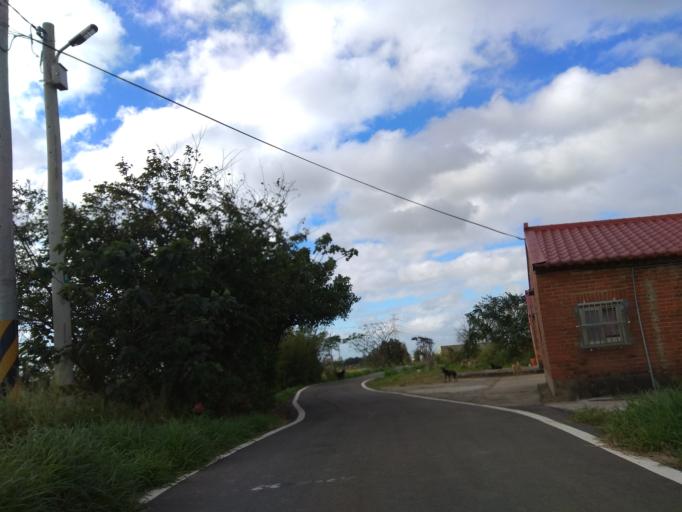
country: TW
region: Taiwan
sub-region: Hsinchu
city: Zhubei
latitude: 24.9687
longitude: 121.0820
